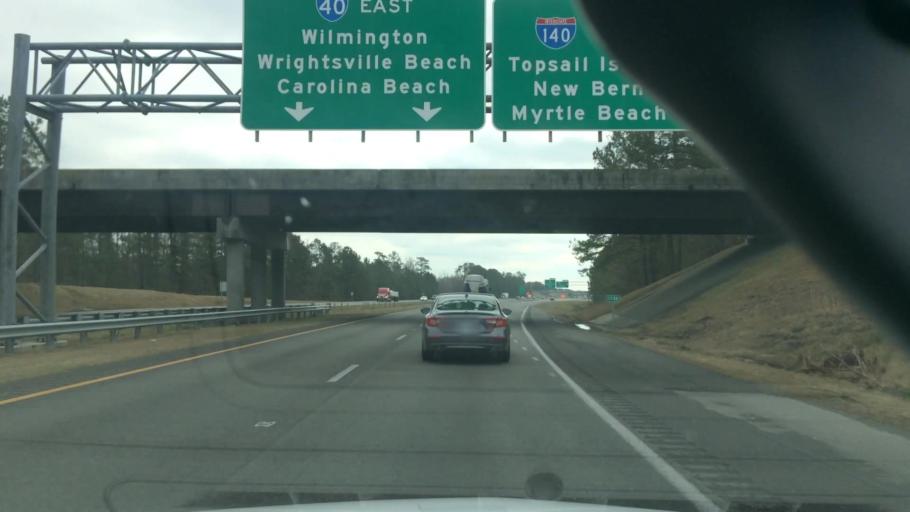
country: US
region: North Carolina
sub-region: New Hanover County
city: Skippers Corner
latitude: 34.3279
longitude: -77.8736
